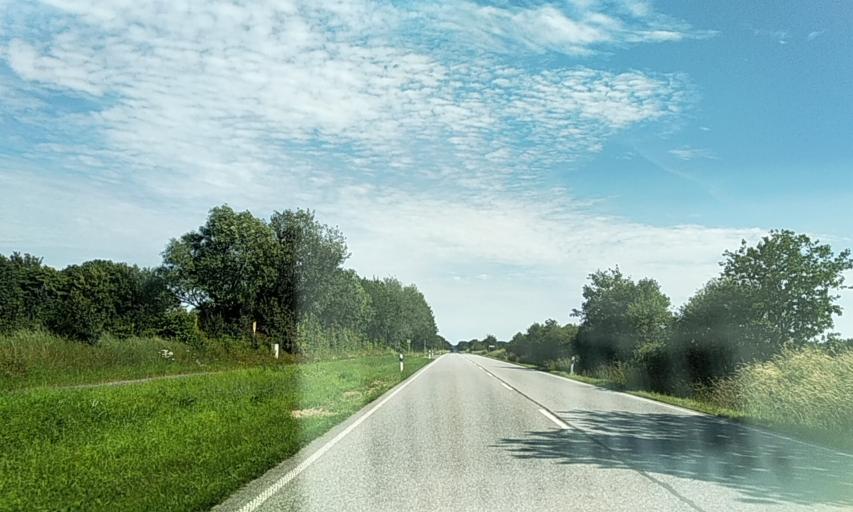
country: DE
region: Schleswig-Holstein
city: Kropp
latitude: 54.4264
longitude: 9.5314
